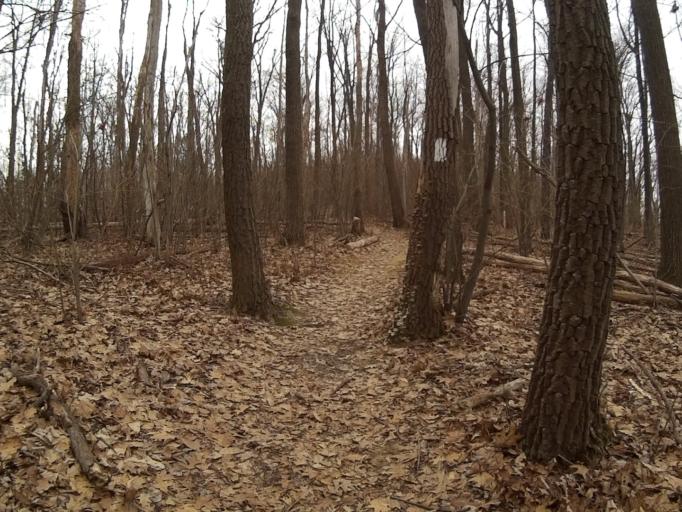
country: US
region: Pennsylvania
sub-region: Centre County
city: Lemont
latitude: 40.8166
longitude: -77.7918
